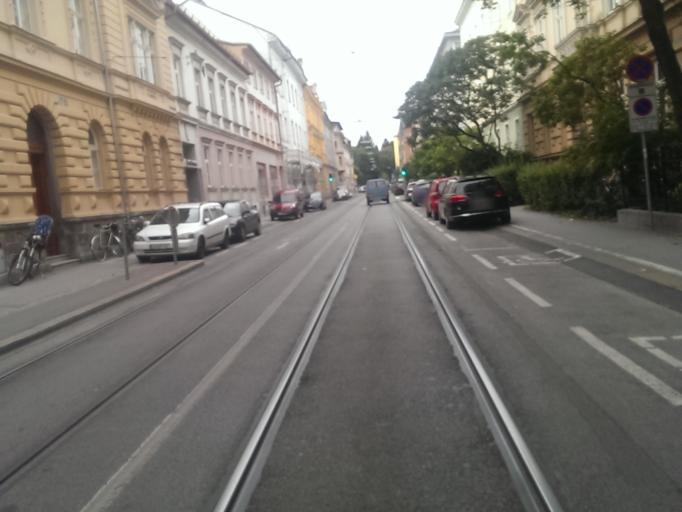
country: AT
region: Styria
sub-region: Graz Stadt
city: Graz
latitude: 47.0689
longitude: 15.4529
